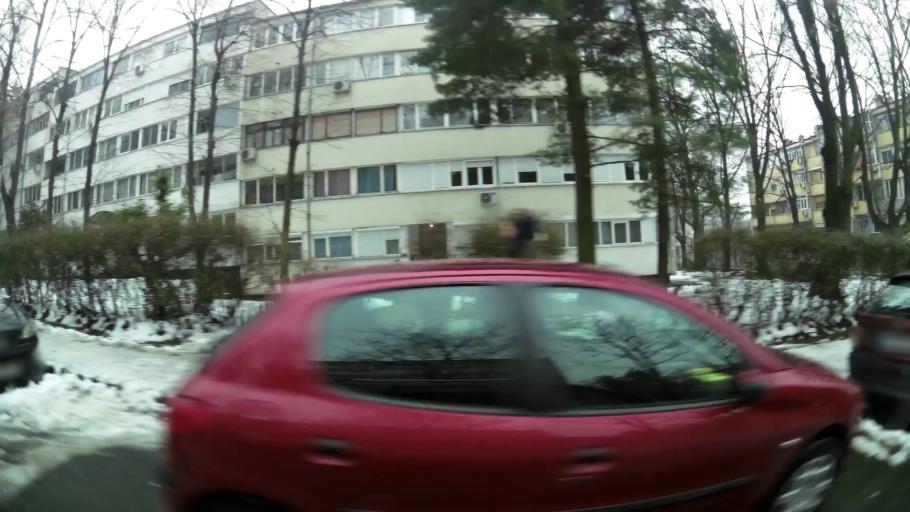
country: RS
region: Central Serbia
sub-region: Belgrade
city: Vozdovac
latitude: 44.7692
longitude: 20.4928
